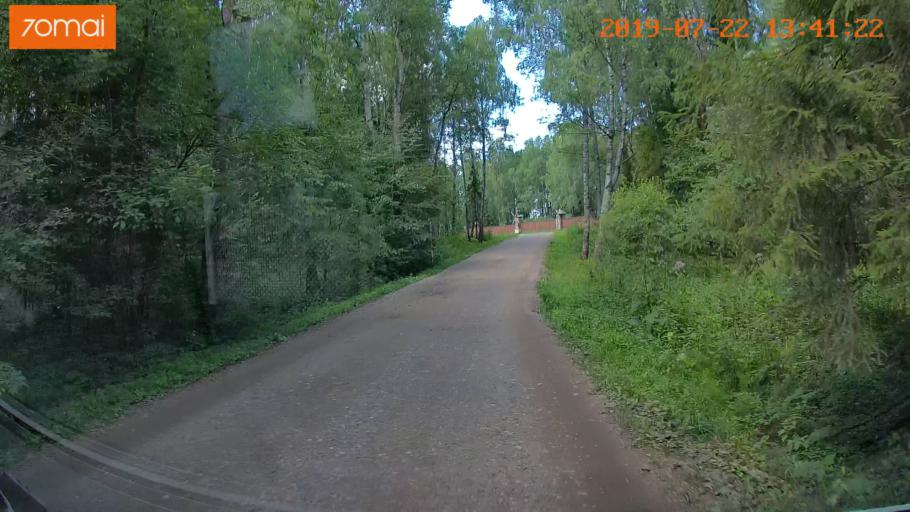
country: RU
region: Ivanovo
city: Novo-Talitsy
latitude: 57.0794
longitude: 40.8794
